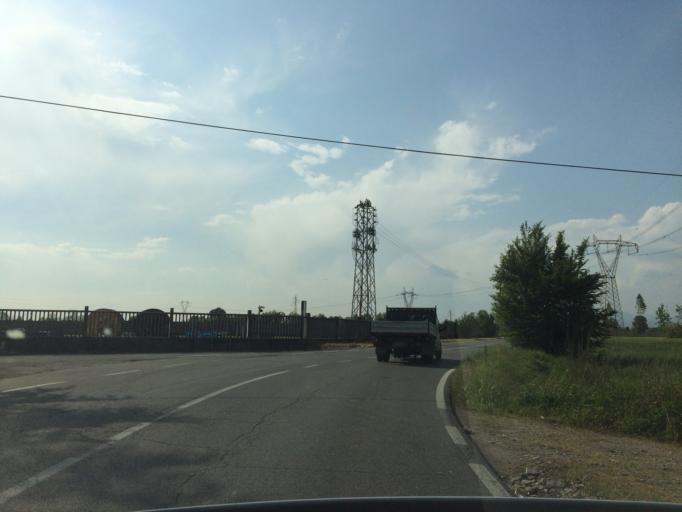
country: IT
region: Lombardy
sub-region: Provincia di Brescia
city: Folzano
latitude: 45.4923
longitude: 10.1940
